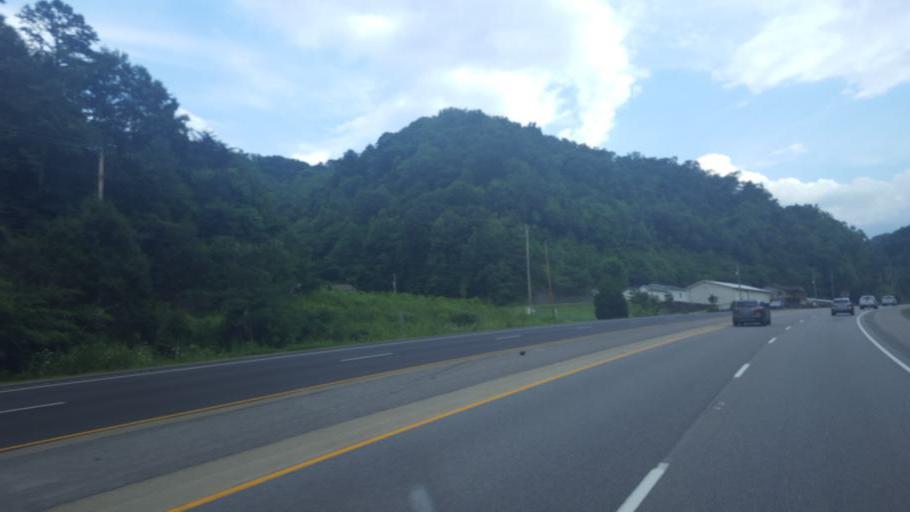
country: US
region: Kentucky
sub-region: Pike County
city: Pikeville
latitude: 37.4307
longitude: -82.5149
